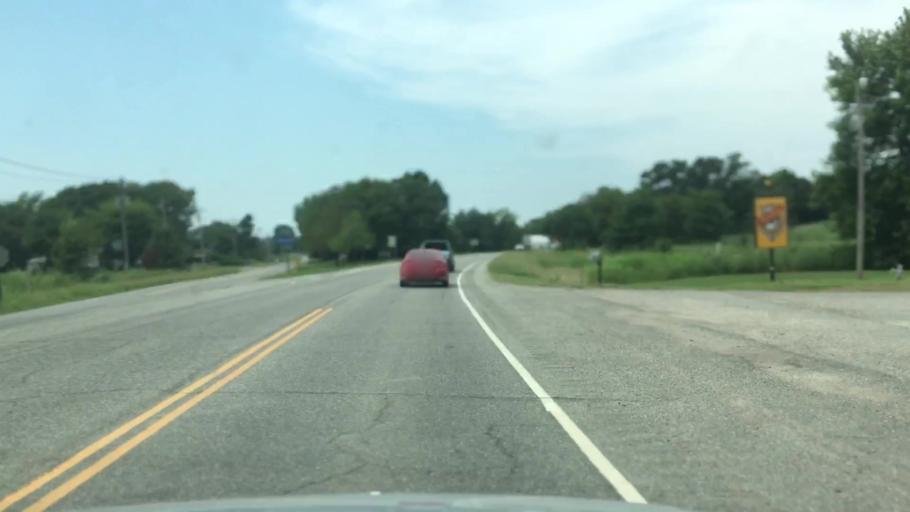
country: US
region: Oklahoma
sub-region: Muskogee County
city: Fort Gibson
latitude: 35.9334
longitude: -95.1544
